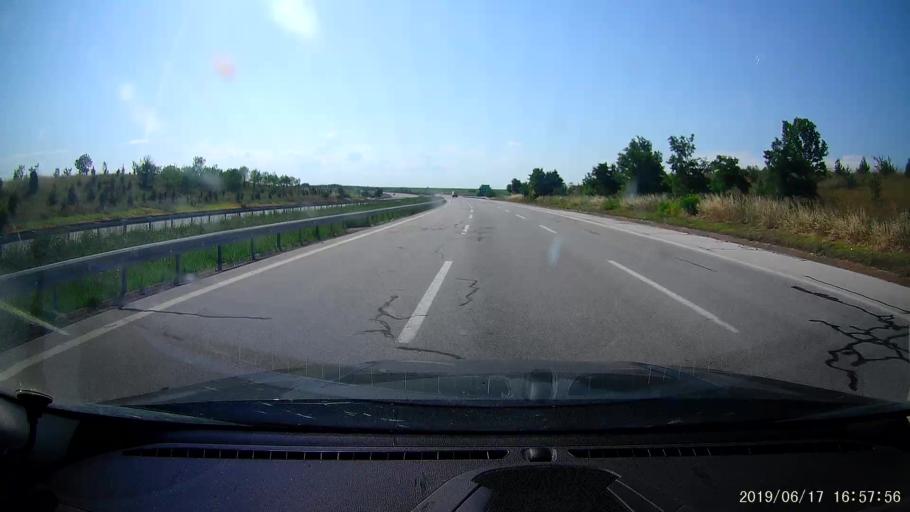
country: TR
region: Edirne
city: Haskoy
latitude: 41.6083
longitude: 26.9026
